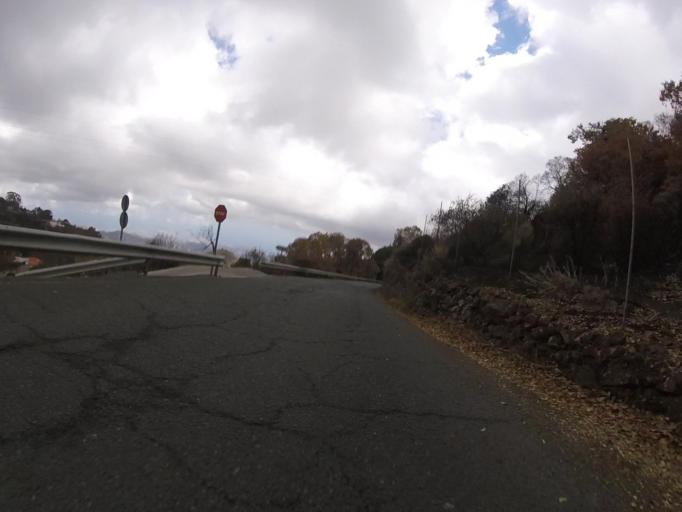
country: ES
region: Canary Islands
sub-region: Provincia de Las Palmas
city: Tejeda
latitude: 27.9840
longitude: -15.5754
